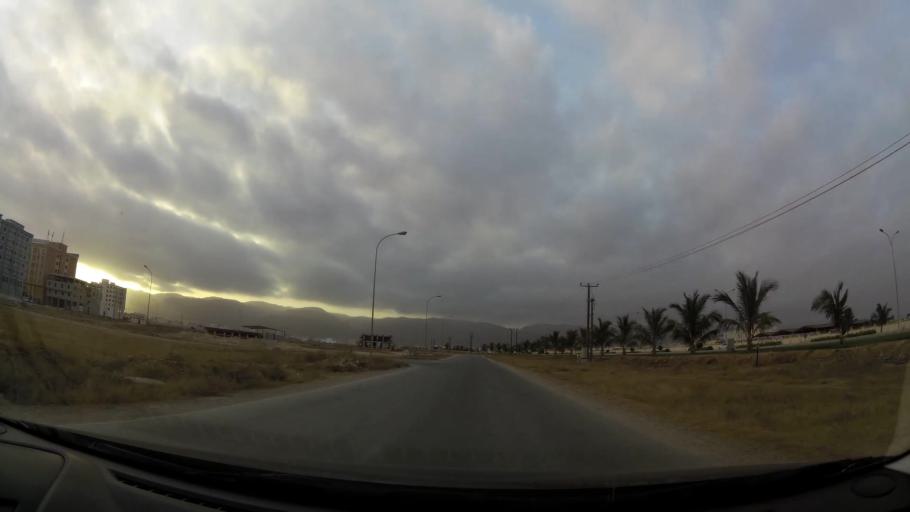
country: OM
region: Zufar
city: Salalah
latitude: 17.0277
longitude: 54.0310
